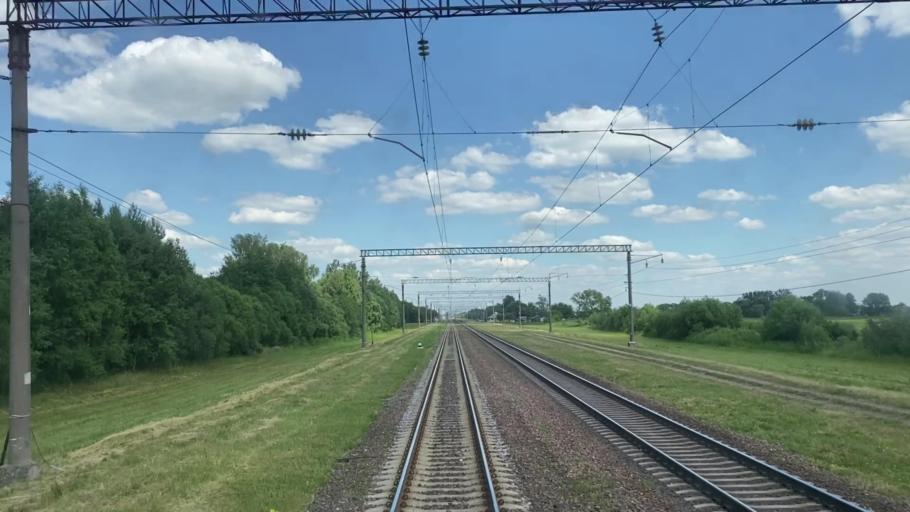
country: BY
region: Brest
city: Charnawchytsy
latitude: 52.1407
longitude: 23.8435
